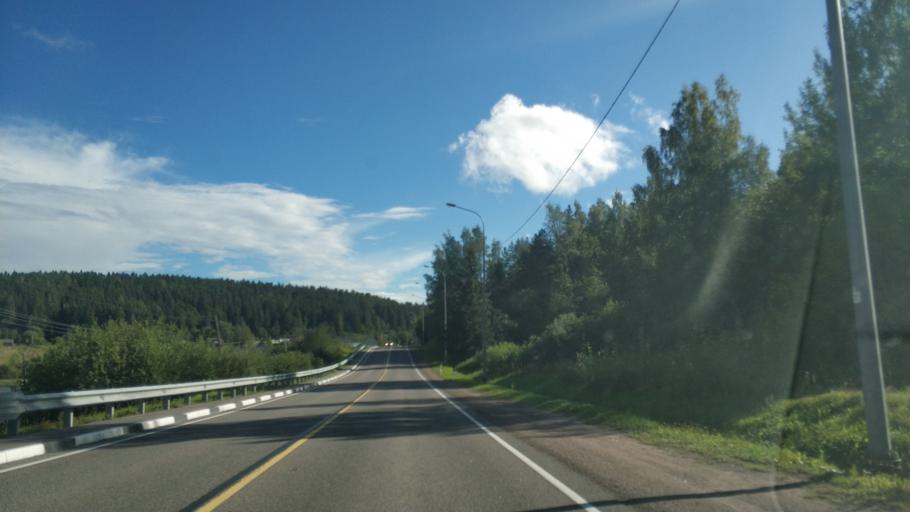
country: RU
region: Republic of Karelia
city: Sortavala
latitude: 61.6630
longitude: 30.6551
